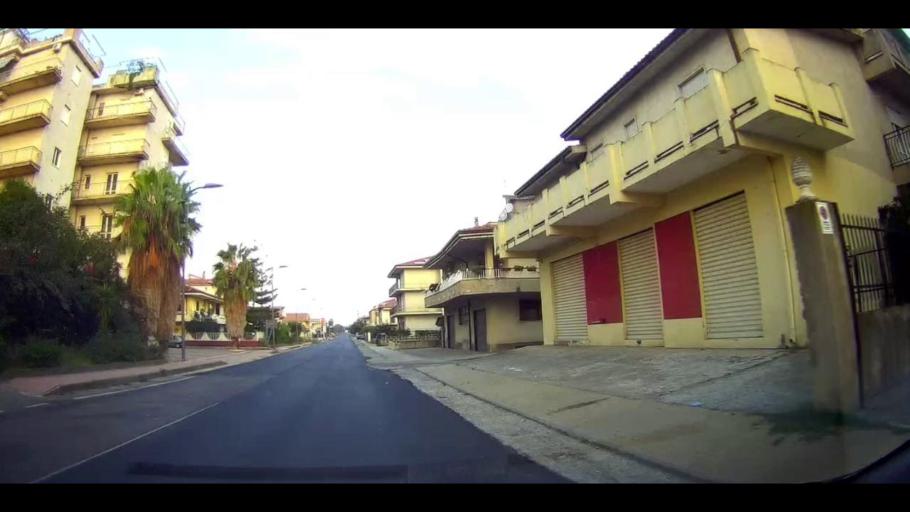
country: IT
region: Calabria
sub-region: Provincia di Crotone
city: Torretta
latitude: 39.4557
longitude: 17.0339
